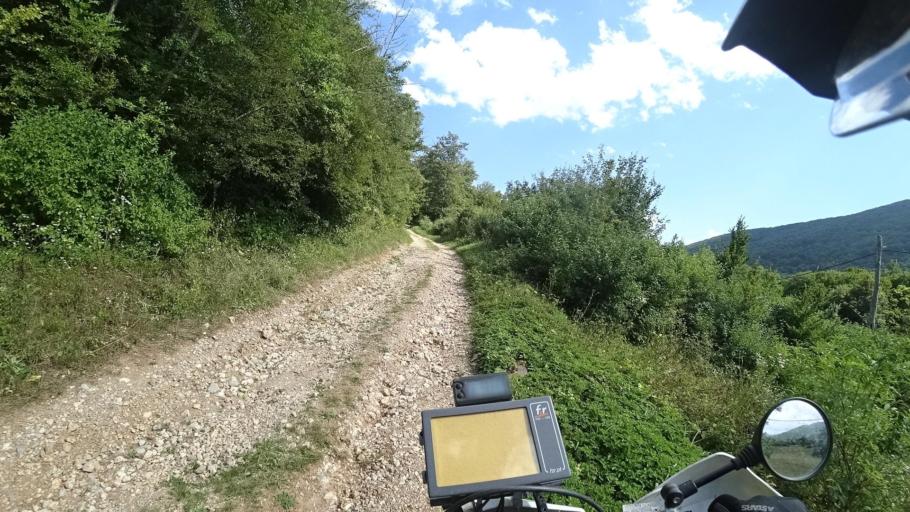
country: HR
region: Licko-Senjska
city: Brinje
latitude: 45.1101
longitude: 15.1074
